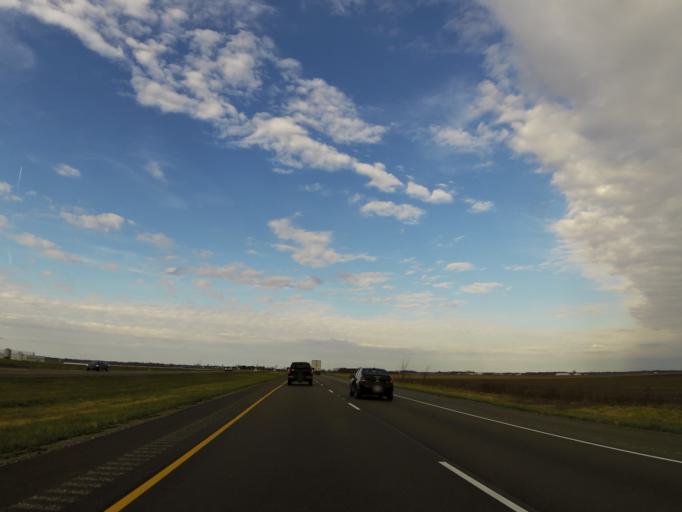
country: US
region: Illinois
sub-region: Washington County
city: Okawville
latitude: 38.4289
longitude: -89.4893
